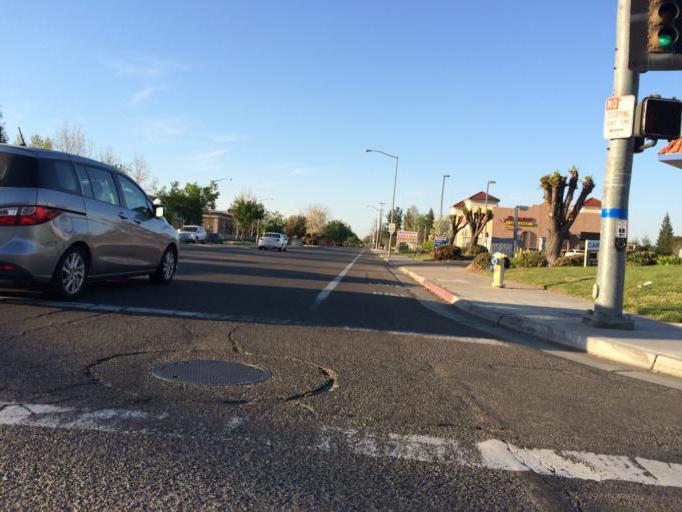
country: US
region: California
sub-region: Fresno County
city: Tarpey Village
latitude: 36.7940
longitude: -119.6821
